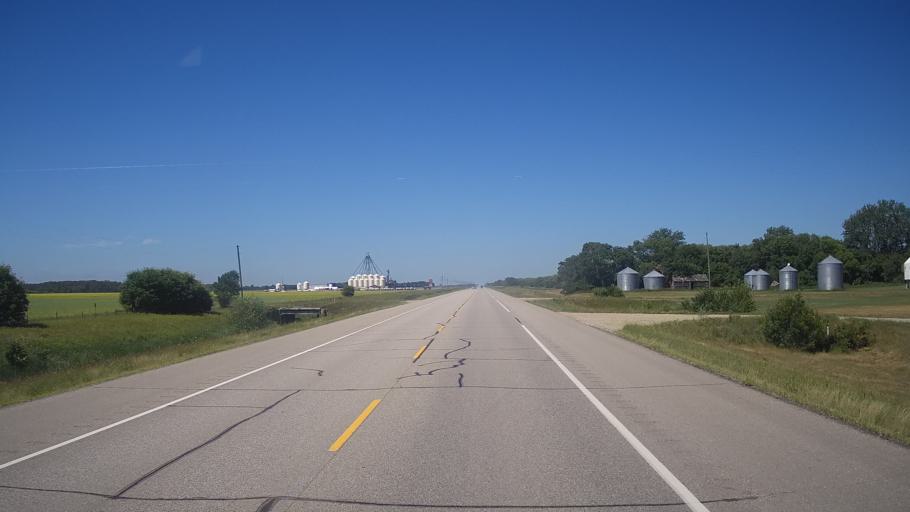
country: CA
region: Manitoba
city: Neepawa
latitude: 50.2257
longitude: -99.0311
